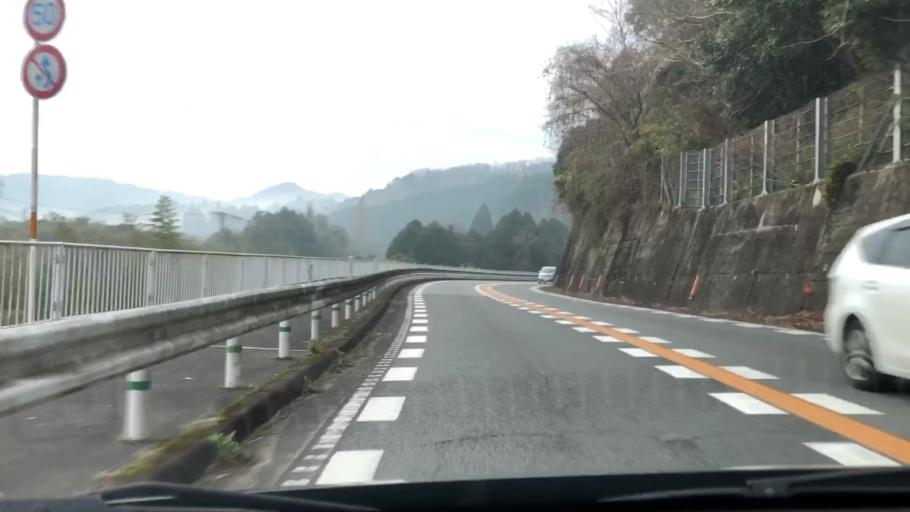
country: JP
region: Oita
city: Usuki
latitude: 33.0265
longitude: 131.6945
